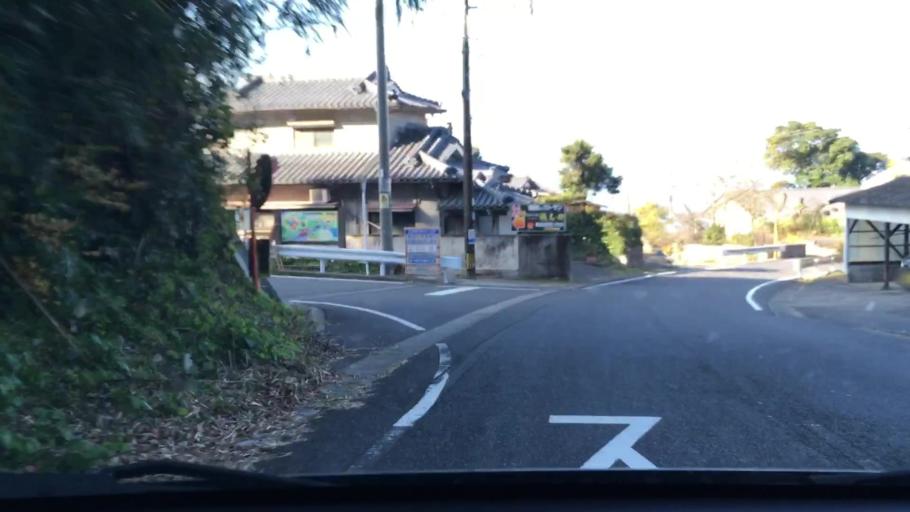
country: JP
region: Kagoshima
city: Kokubu-matsuki
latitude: 31.6702
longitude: 130.8201
